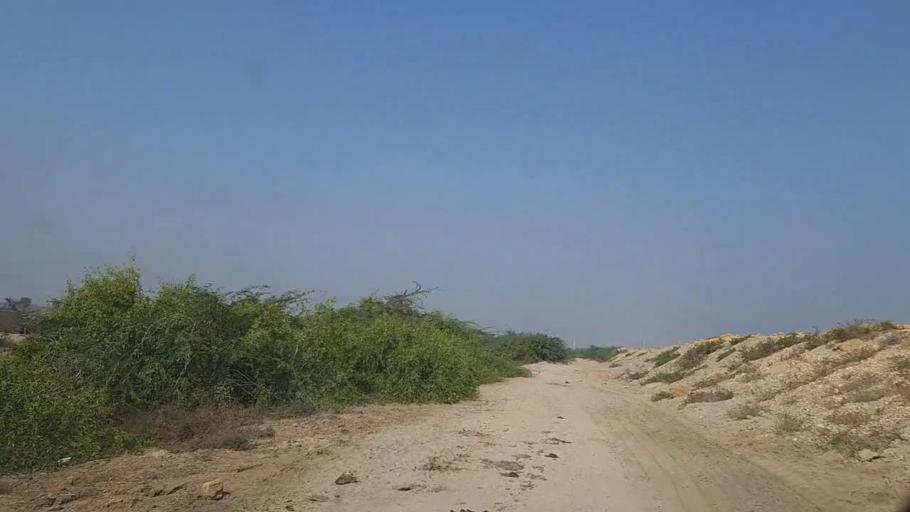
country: PK
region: Sindh
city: Thatta
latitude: 24.6597
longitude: 67.9266
